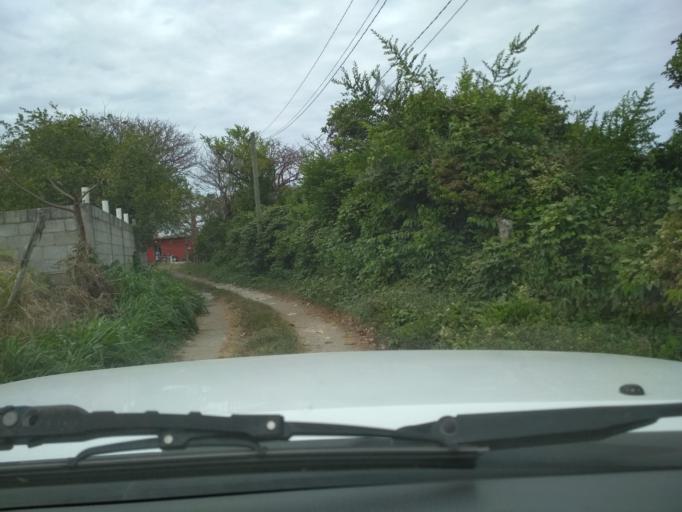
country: MX
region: Veracruz
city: Anton Lizardo
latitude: 19.0542
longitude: -95.9858
